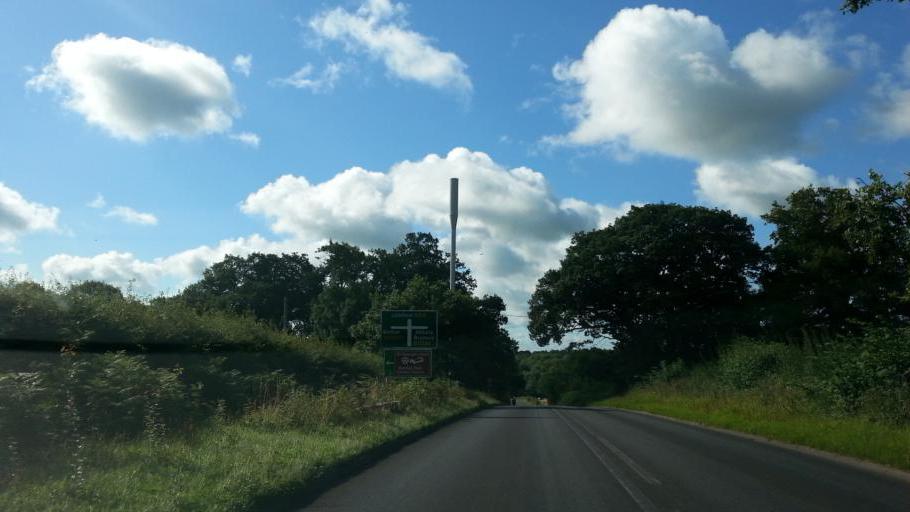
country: GB
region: England
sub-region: Staffordshire
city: Barton under Needwood
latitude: 52.8230
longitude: -1.7799
